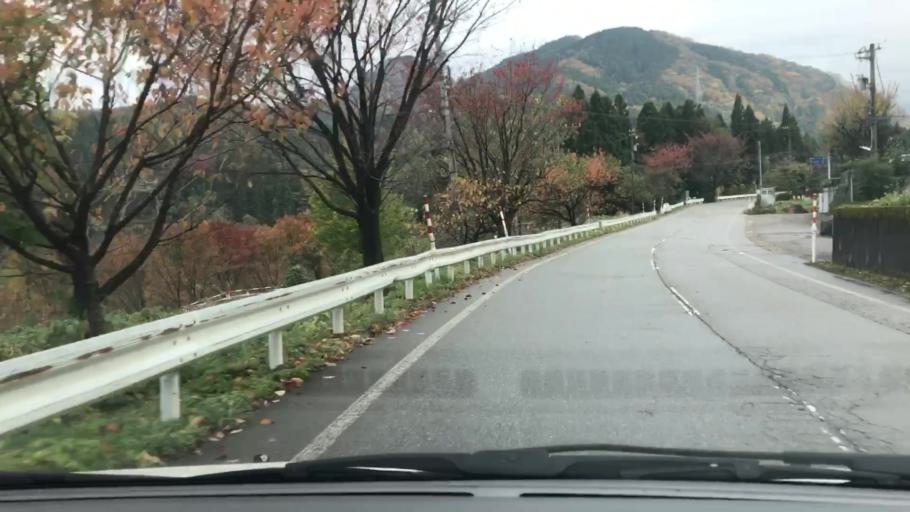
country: JP
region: Toyama
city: Kamiichi
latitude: 36.5814
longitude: 137.3297
